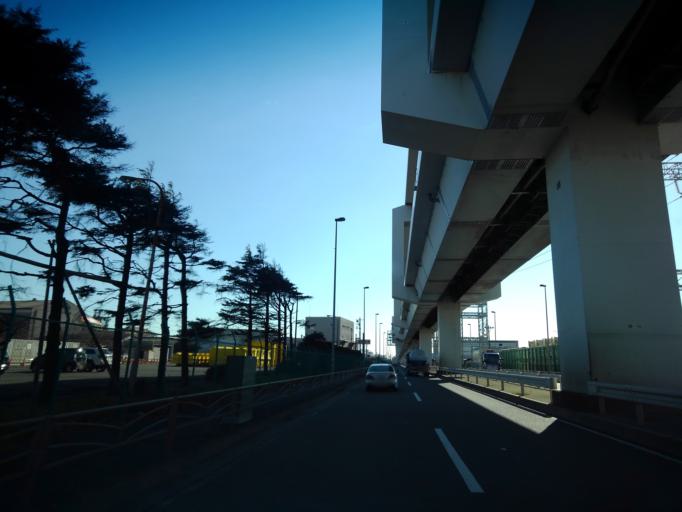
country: JP
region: Kanagawa
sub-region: Kawasaki-shi
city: Kawasaki
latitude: 35.5308
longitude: 139.7704
